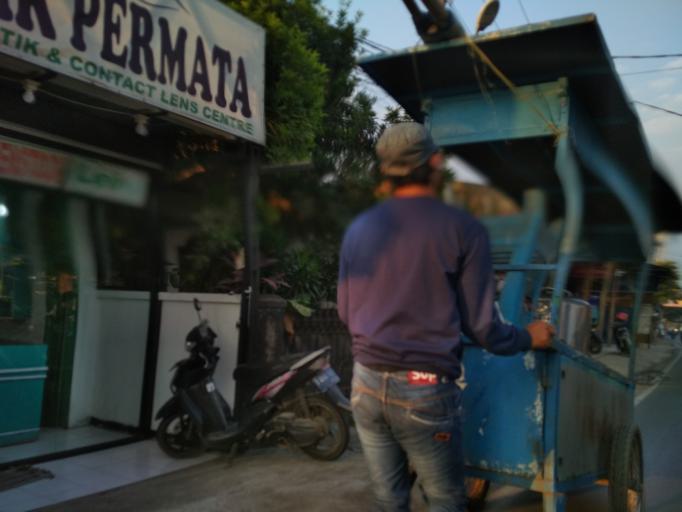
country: ID
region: West Java
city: Ciampea
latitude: -6.5630
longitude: 106.7186
